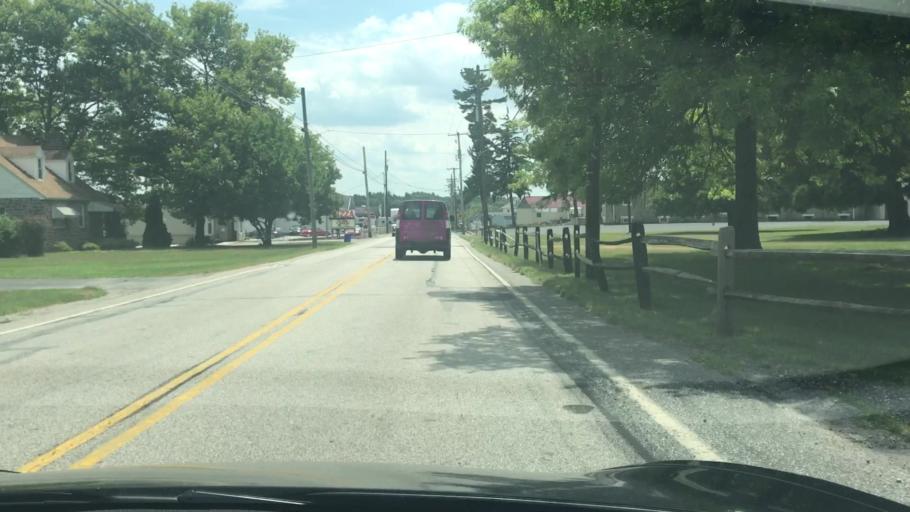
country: US
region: Pennsylvania
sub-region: York County
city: Manchester
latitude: 40.0536
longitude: -76.7667
